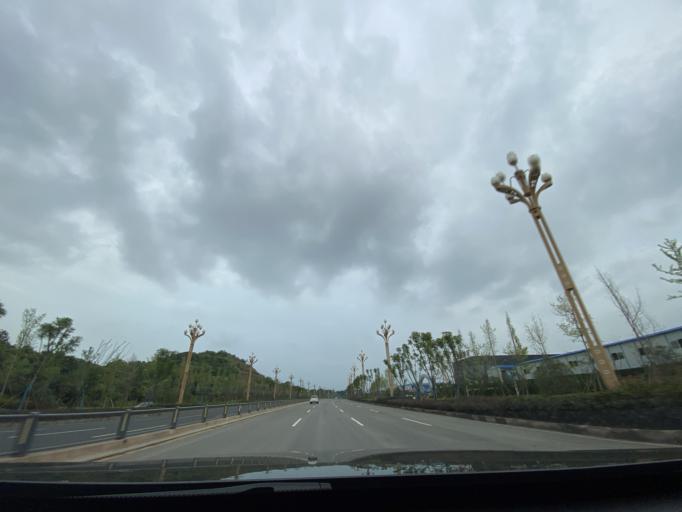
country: CN
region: Sichuan
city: Jiancheng
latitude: 30.4845
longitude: 104.4812
